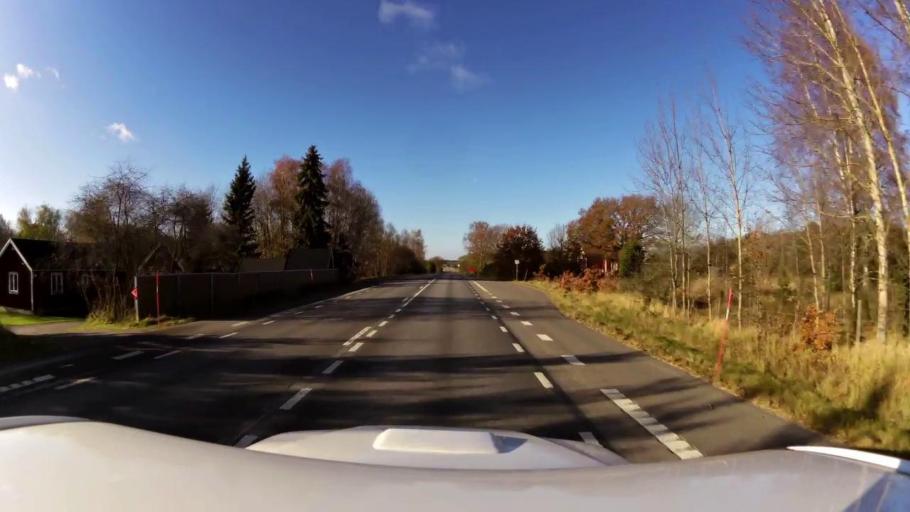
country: SE
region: OEstergoetland
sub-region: Linkopings Kommun
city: Linghem
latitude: 58.4368
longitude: 15.7682
